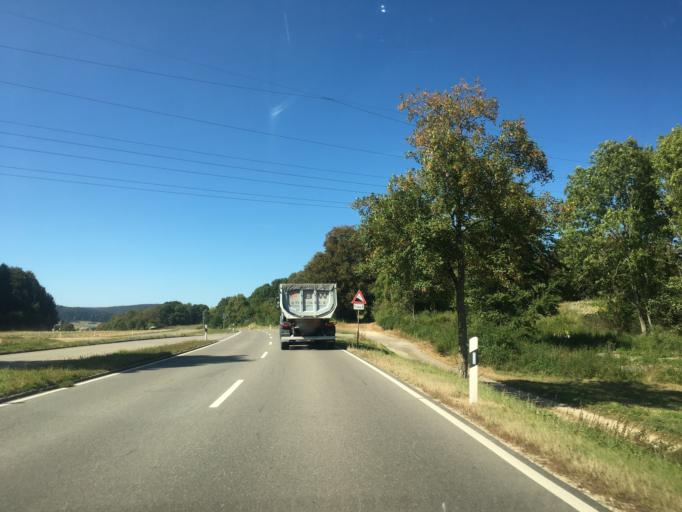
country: DE
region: Baden-Wuerttemberg
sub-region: Tuebingen Region
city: Sankt Johann
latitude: 48.3807
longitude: 9.3111
